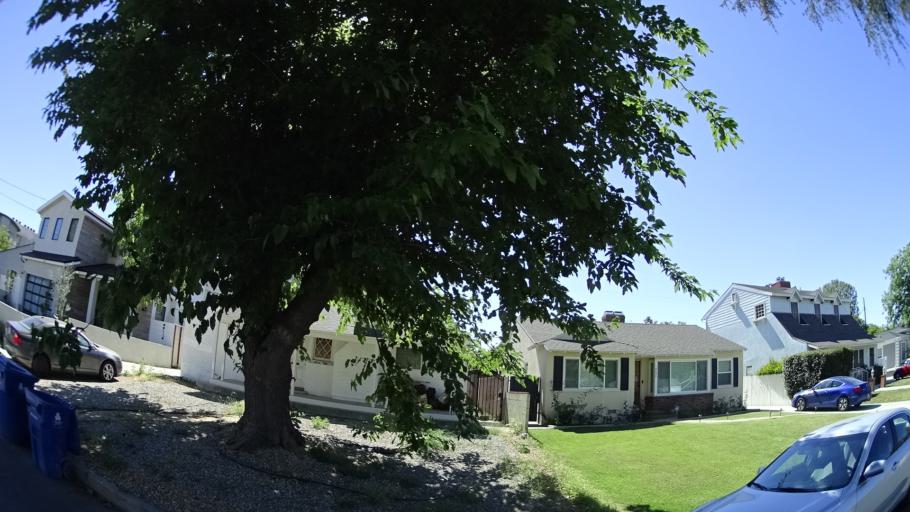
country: US
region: California
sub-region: Los Angeles County
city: Sherman Oaks
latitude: 34.1547
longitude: -118.4618
